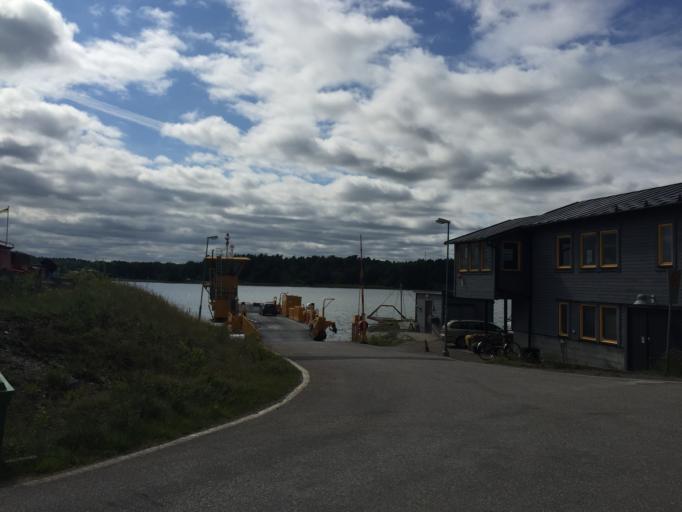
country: SE
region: Soedermanland
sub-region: Trosa Kommun
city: Trosa
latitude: 58.9716
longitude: 17.7124
